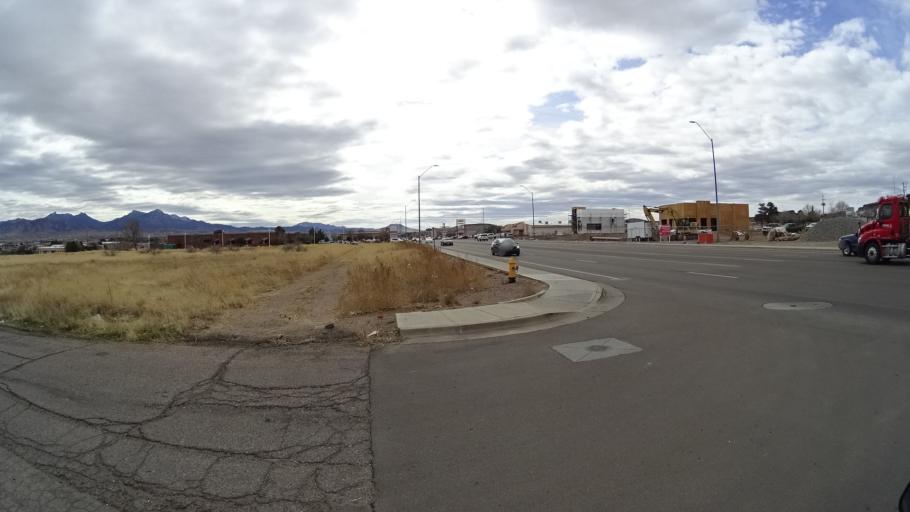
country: US
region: Arizona
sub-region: Mohave County
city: New Kingman-Butler
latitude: 35.2310
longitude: -114.0366
